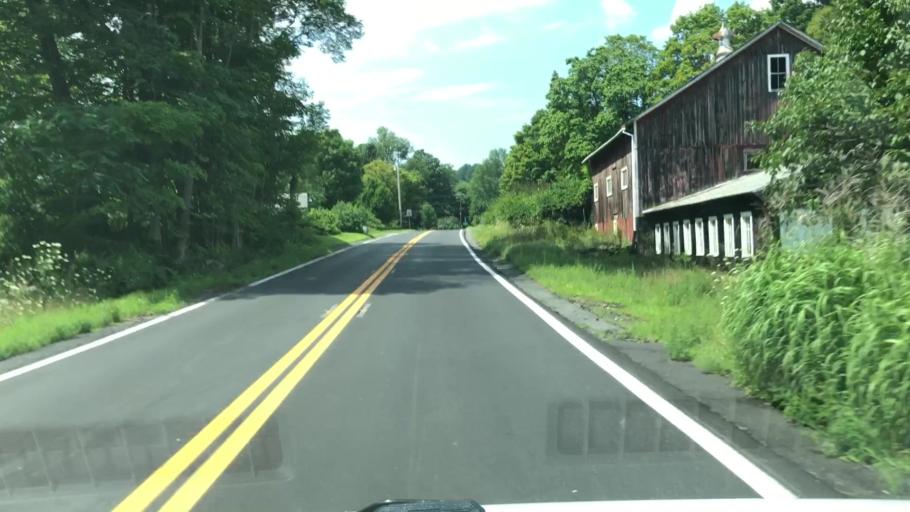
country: US
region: Massachusetts
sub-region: Franklin County
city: Ashfield
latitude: 42.5097
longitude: -72.7730
